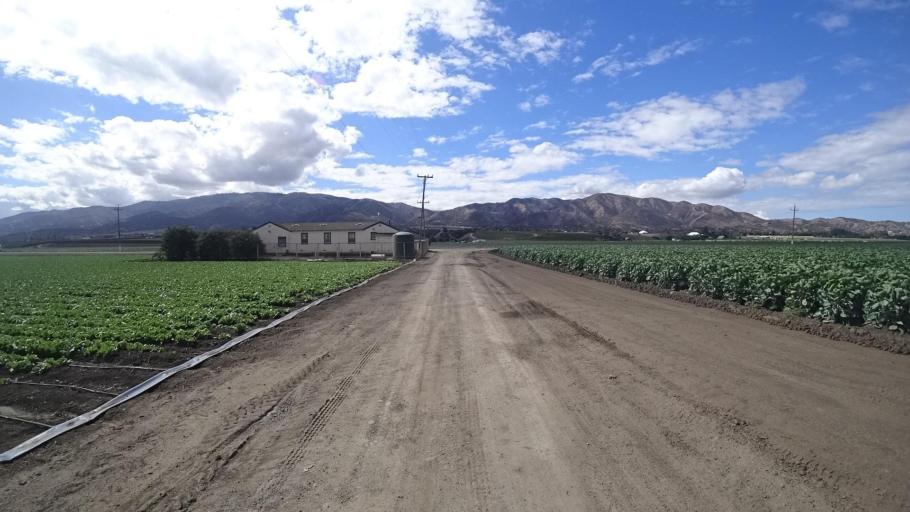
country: US
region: California
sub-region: Monterey County
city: Salinas
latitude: 36.6014
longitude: -121.6113
